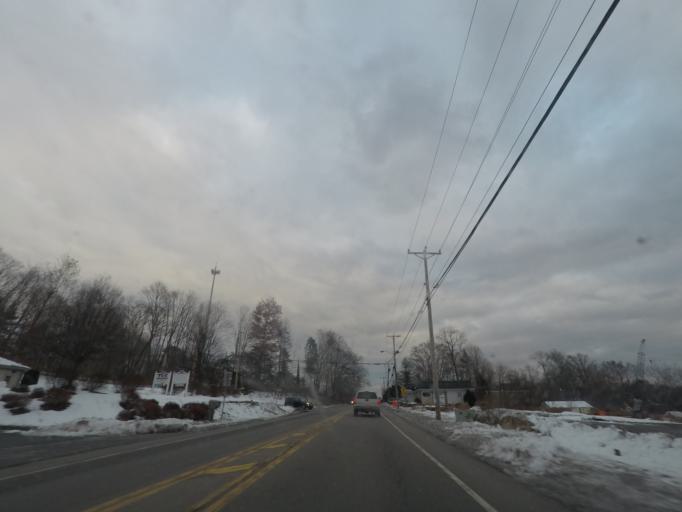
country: US
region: New York
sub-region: Orange County
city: Gardnertown
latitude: 41.5509
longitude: -74.0617
